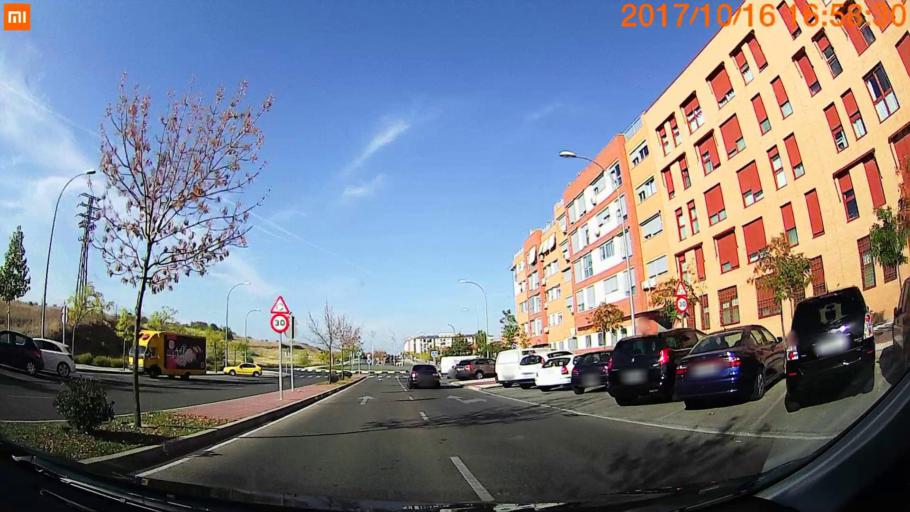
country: ES
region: Madrid
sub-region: Provincia de Madrid
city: Alcobendas
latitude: 40.5519
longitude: -3.6622
